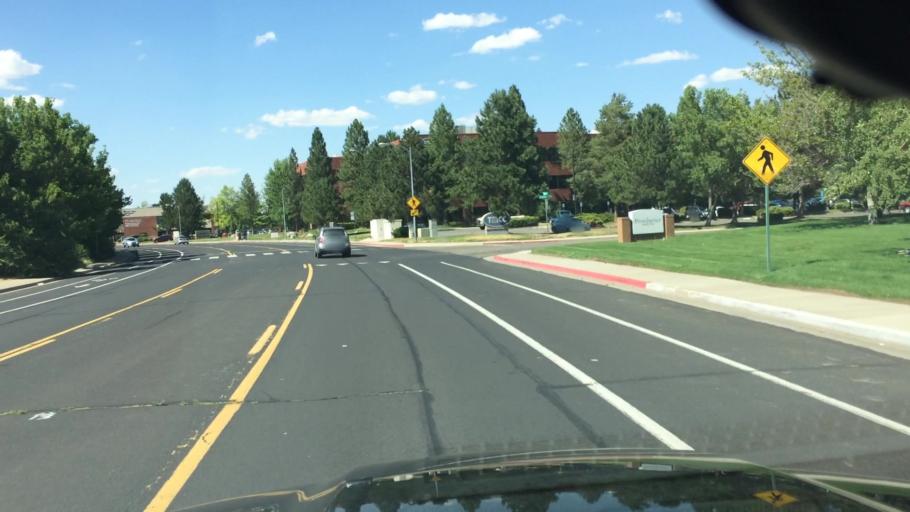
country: US
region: Nevada
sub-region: Washoe County
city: Reno
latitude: 39.4728
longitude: -119.7786
